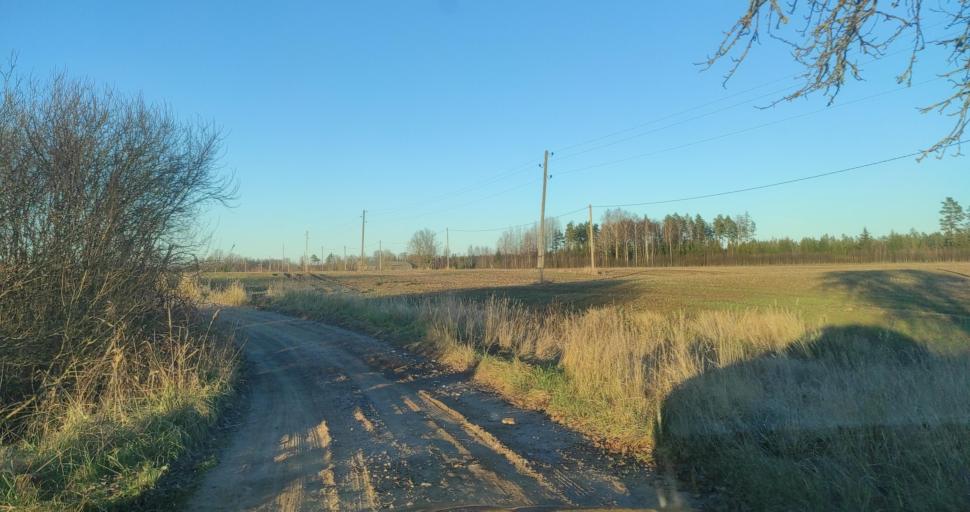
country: LV
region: Dundaga
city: Dundaga
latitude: 57.3869
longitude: 22.0885
